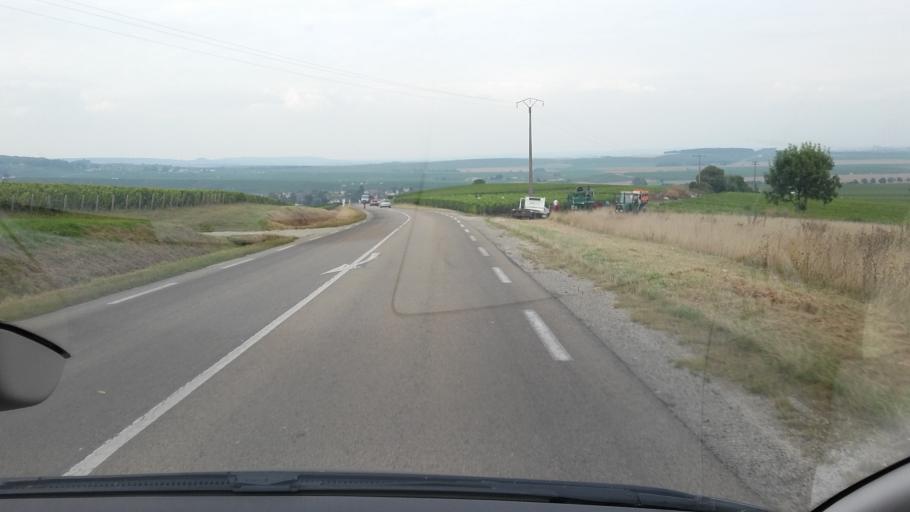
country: FR
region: Champagne-Ardenne
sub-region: Departement de la Marne
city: Verzenay
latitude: 49.1527
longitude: 4.0954
